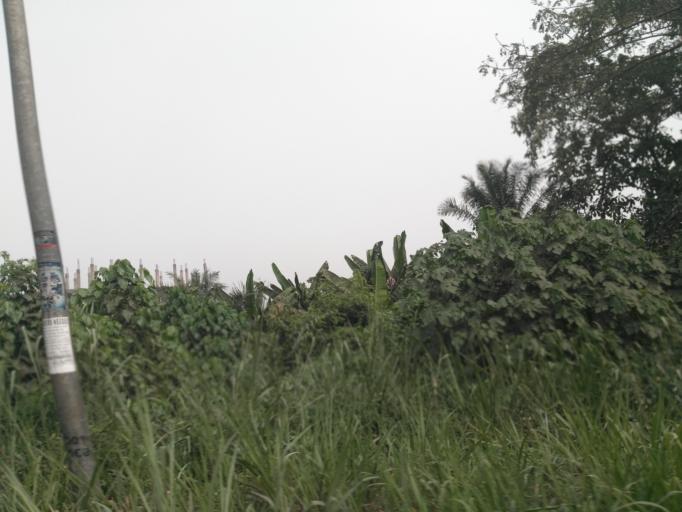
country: GH
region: Ashanti
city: Kumasi
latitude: 6.6865
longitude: -1.6286
